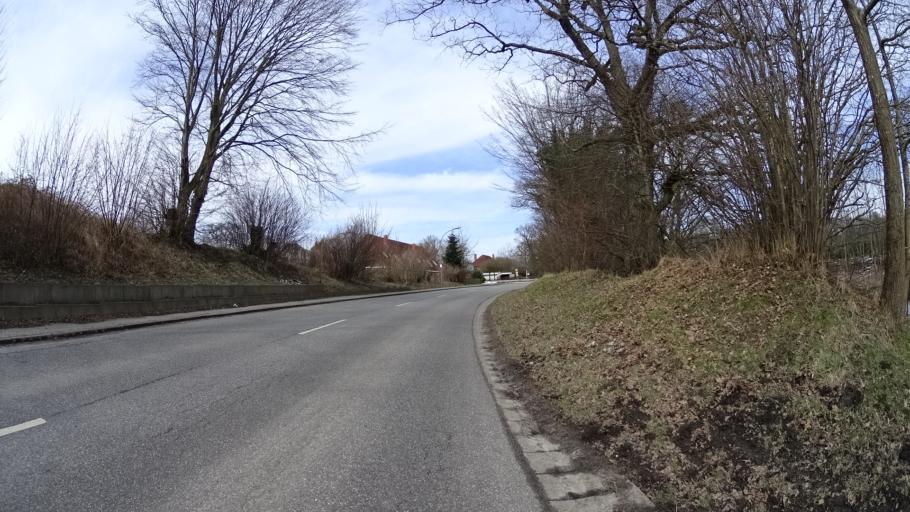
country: DE
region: Schleswig-Holstein
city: Kuhren
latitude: 54.2011
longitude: 10.2604
